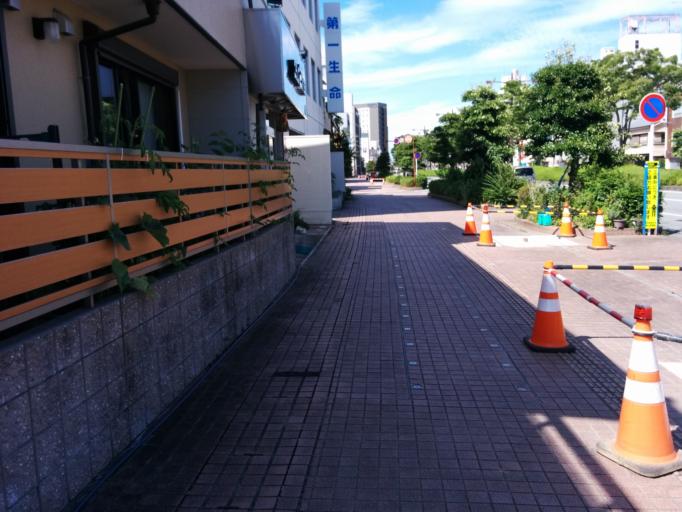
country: JP
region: Mie
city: Ise
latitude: 34.4887
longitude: 136.7064
